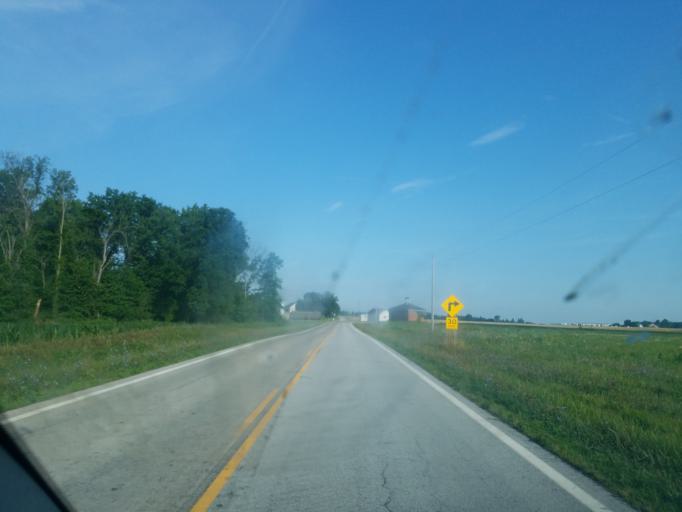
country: US
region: Ohio
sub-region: Hardin County
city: Forest
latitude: 40.7765
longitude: -83.4658
